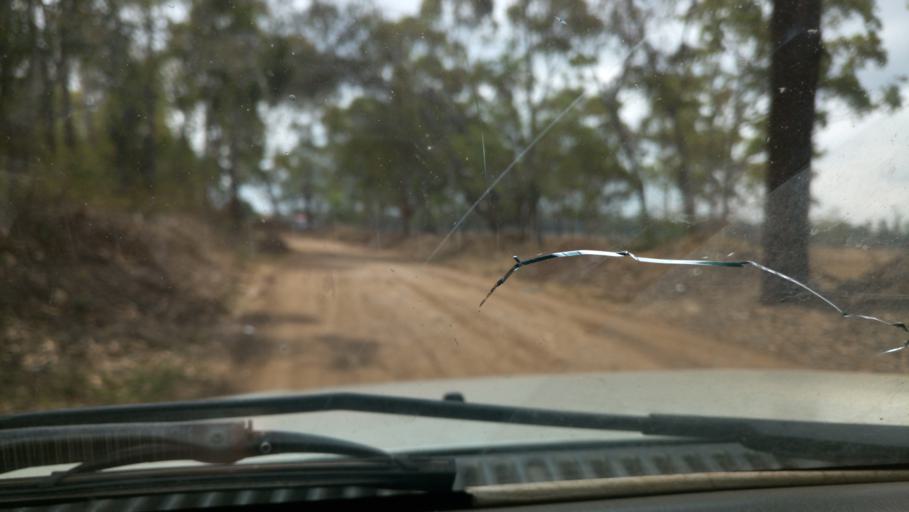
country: KE
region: Nairobi Area
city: Nairobi
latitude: -1.3313
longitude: 36.7520
